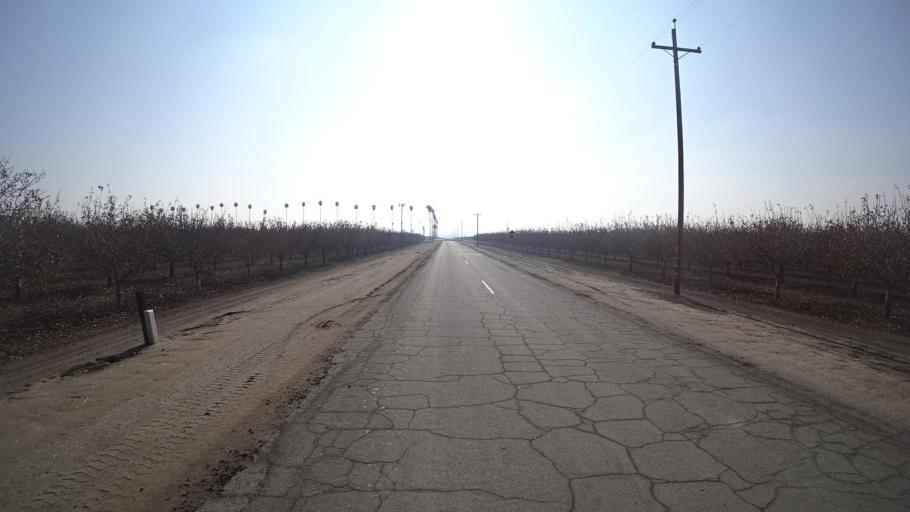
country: US
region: California
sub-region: Kern County
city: Buttonwillow
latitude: 35.3422
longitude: -119.3944
